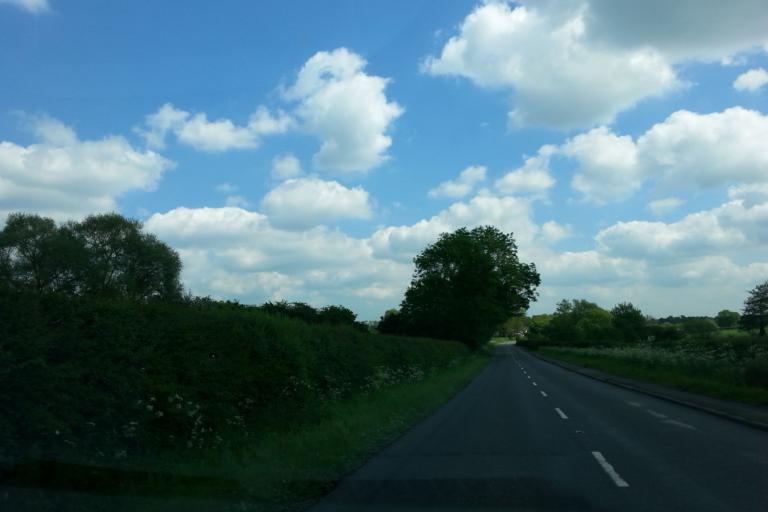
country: GB
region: England
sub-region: Cambridgeshire
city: Stilton
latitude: 52.4984
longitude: -0.3069
